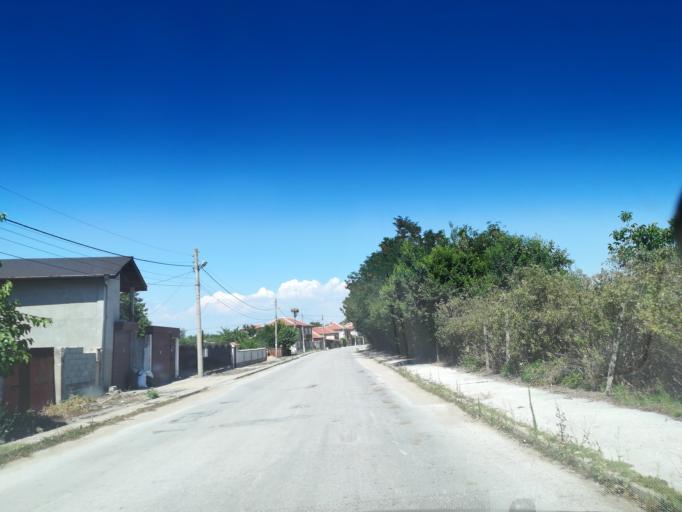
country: BG
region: Plovdiv
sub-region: Obshtina Sadovo
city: Sadovo
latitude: 42.0230
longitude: 25.1023
